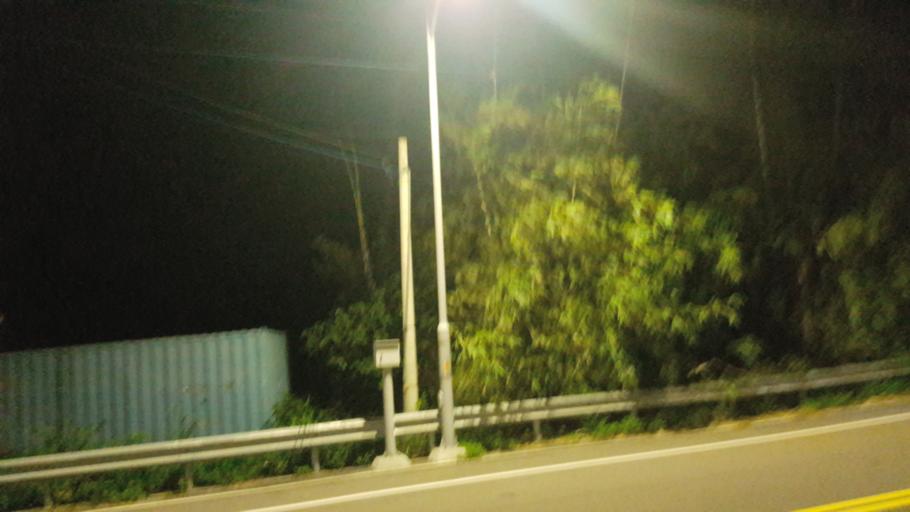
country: TW
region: Taiwan
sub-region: Hsinchu
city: Hsinchu
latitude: 24.7499
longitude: 120.9680
